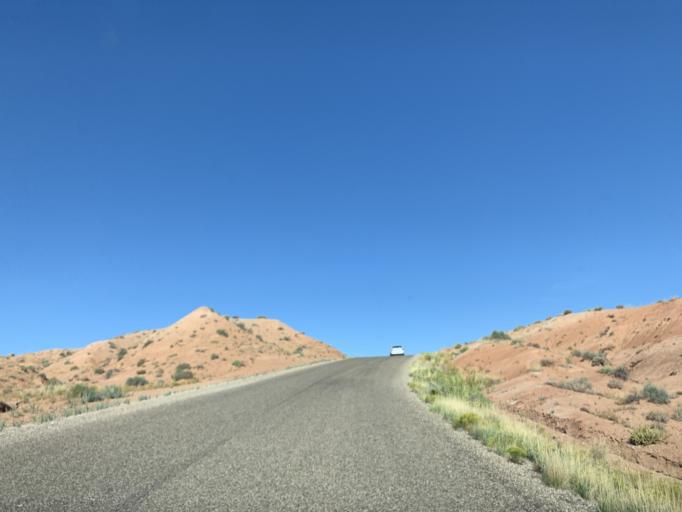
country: US
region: Utah
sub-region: Emery County
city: Ferron
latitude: 38.5818
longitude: -110.7820
